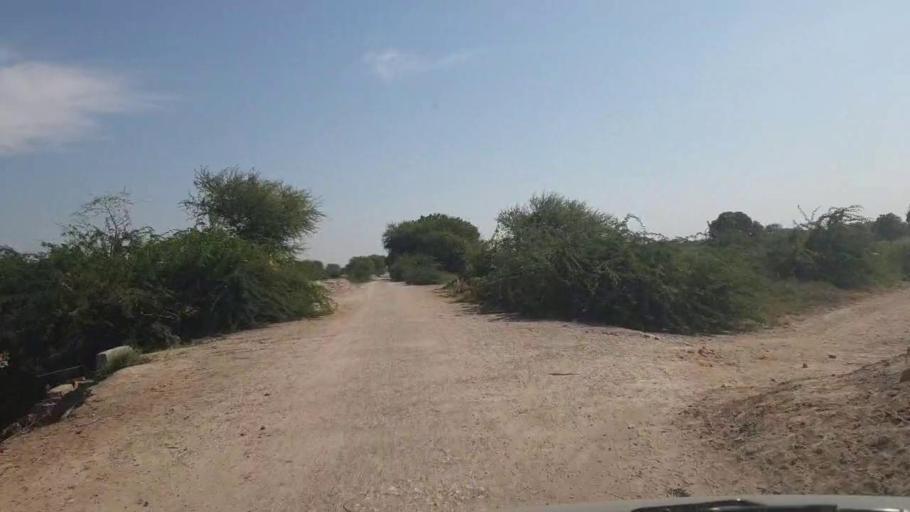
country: PK
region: Sindh
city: Digri
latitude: 24.9524
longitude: 69.1448
